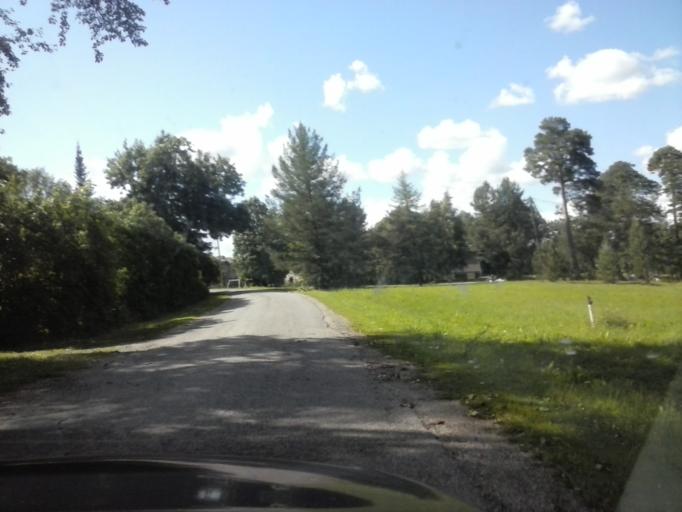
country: EE
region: Laeaene-Virumaa
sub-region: Vaeike-Maarja vald
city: Vaike-Maarja
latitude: 59.0861
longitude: 26.1813
